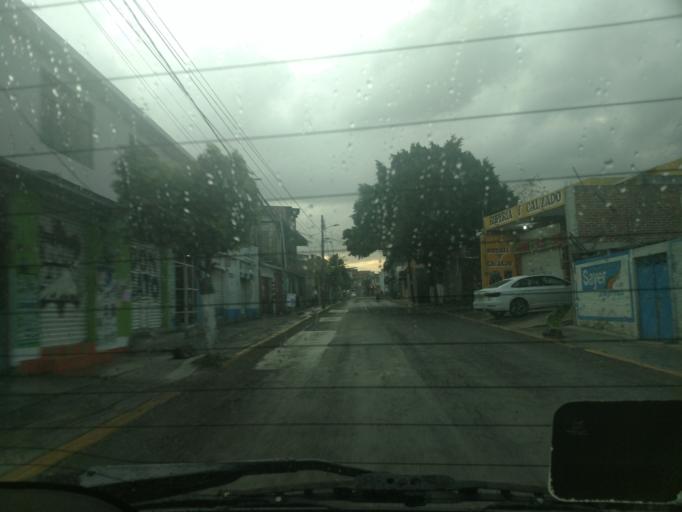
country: MX
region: Morelos
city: Coyotepec
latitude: 19.7743
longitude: -99.2061
